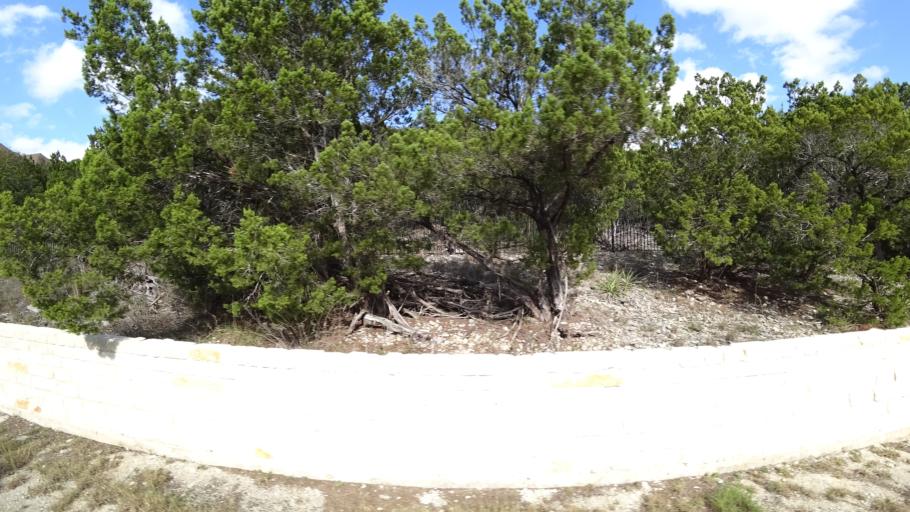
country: US
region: Texas
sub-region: Williamson County
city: Anderson Mill
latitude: 30.4199
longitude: -97.8045
